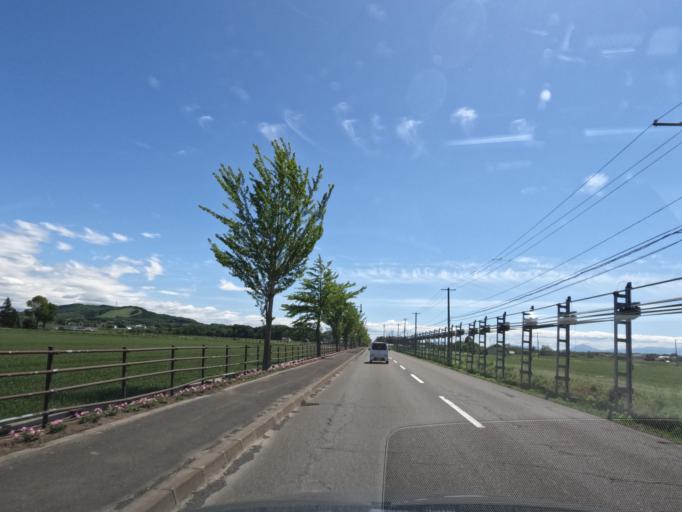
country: JP
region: Hokkaido
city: Iwamizawa
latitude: 43.0683
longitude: 141.7402
